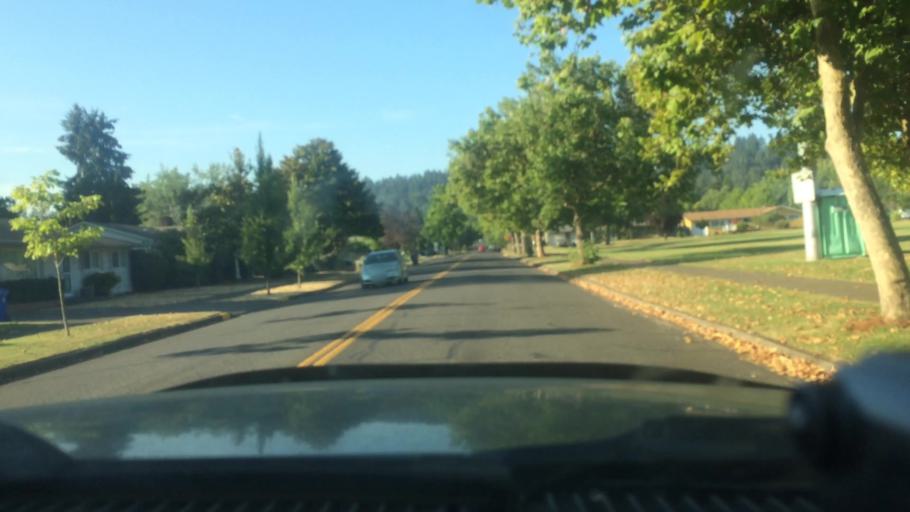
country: US
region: Oregon
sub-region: Lane County
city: Eugene
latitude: 44.0343
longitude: -123.1123
